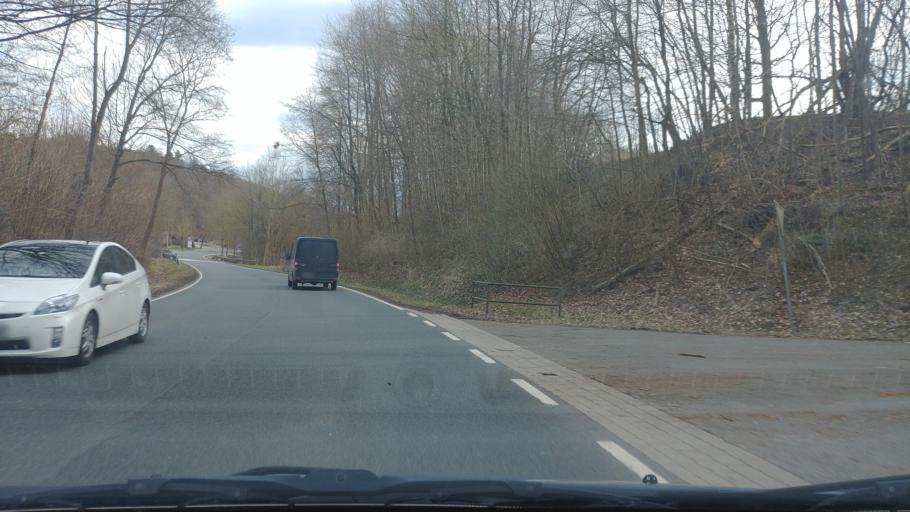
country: DE
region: Lower Saxony
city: Bevern
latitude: 51.8210
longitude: 9.4850
